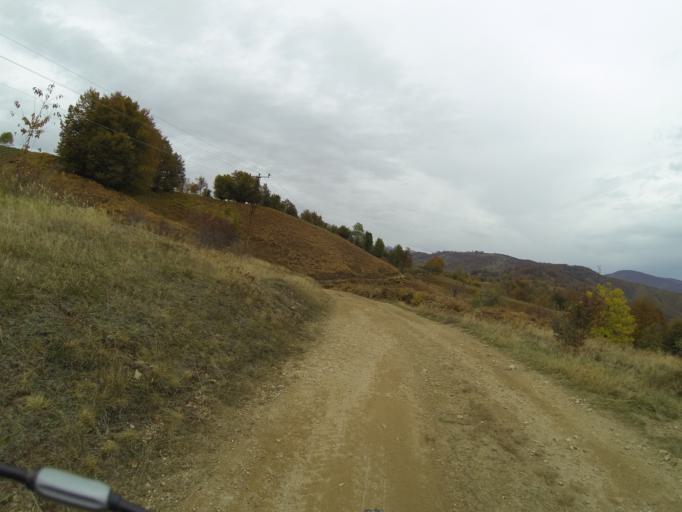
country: RO
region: Gorj
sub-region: Comuna Pades
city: Closani
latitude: 45.1148
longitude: 22.8492
